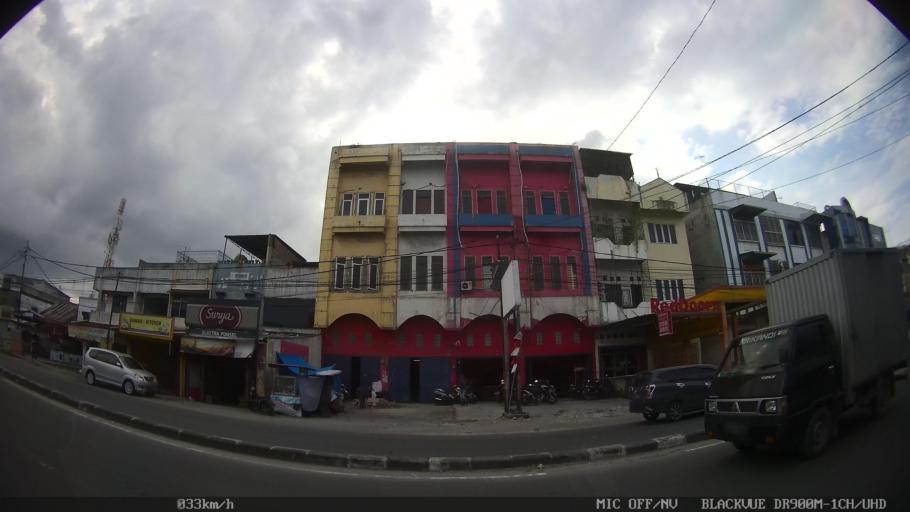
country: ID
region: North Sumatra
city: Medan
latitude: 3.6090
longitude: 98.6742
